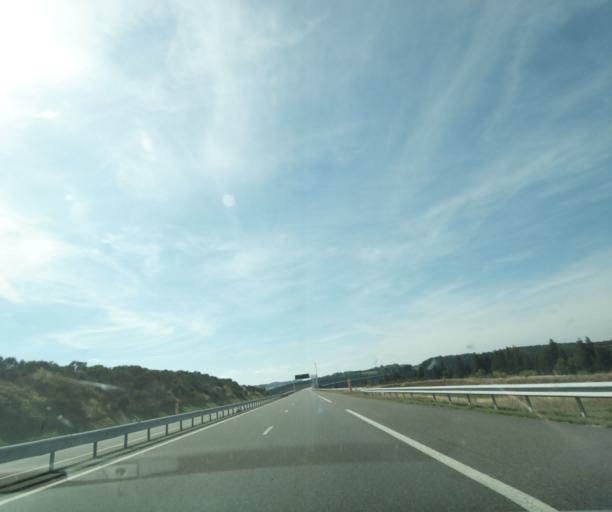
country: FR
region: Auvergne
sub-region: Departement du Puy-de-Dome
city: Saint-Ours
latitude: 45.8573
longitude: 2.8651
